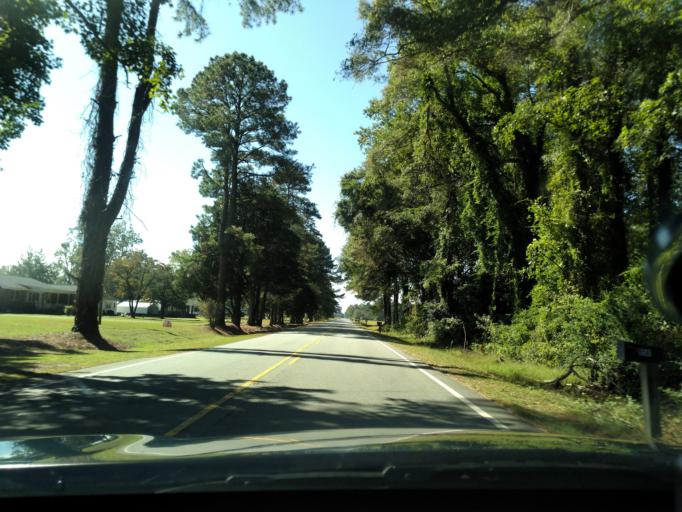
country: US
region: North Carolina
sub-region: Washington County
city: Plymouth
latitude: 35.7288
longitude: -76.7477
